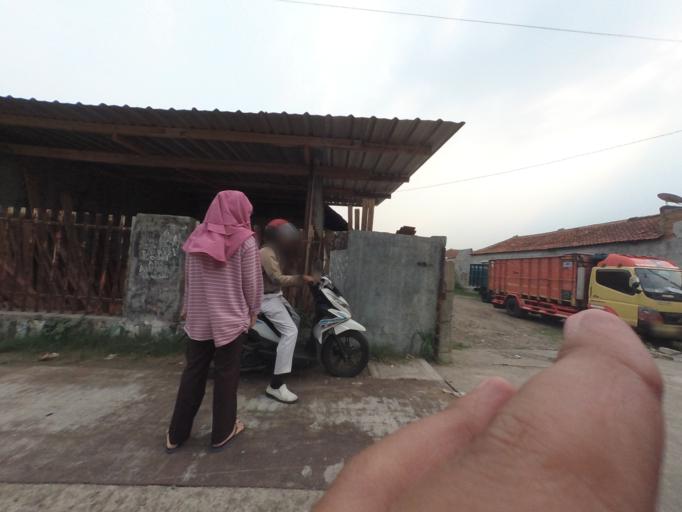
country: ID
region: West Java
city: Sidoger Lebak
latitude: -6.5664
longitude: 106.5955
